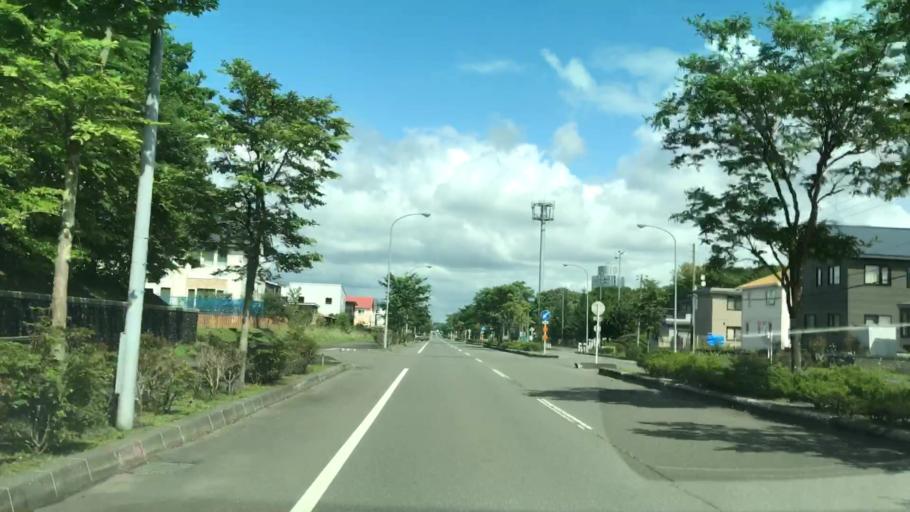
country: JP
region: Hokkaido
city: Chitose
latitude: 42.7765
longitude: 141.5996
